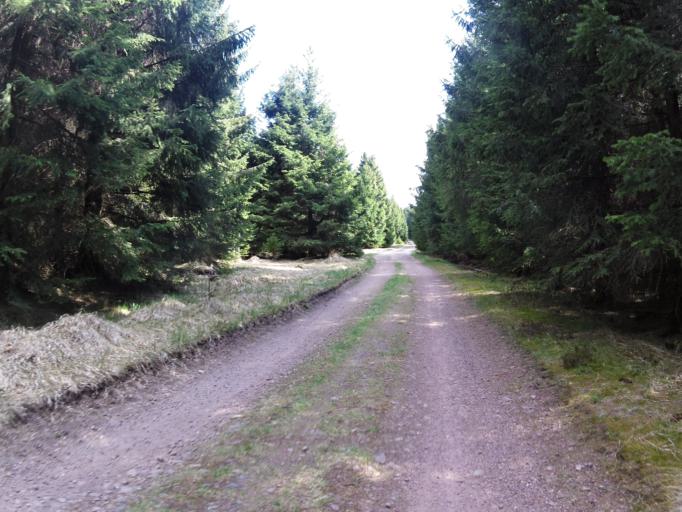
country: DE
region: Thuringia
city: Bermbach
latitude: 50.7189
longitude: 10.6464
